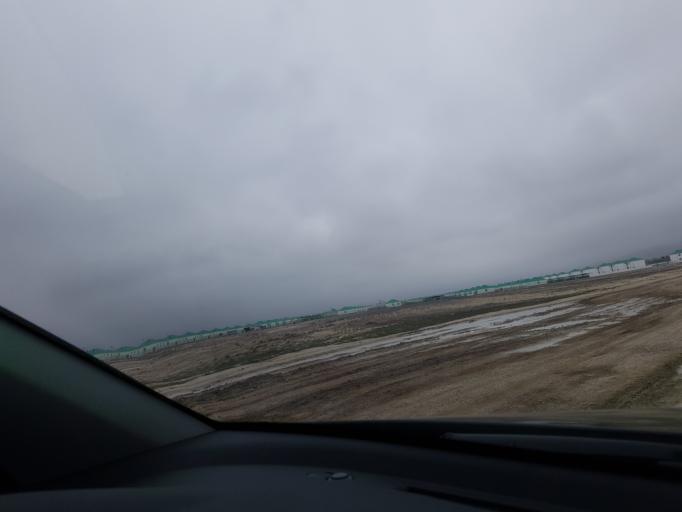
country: TM
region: Ahal
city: Abadan
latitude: 38.1424
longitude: 57.9552
